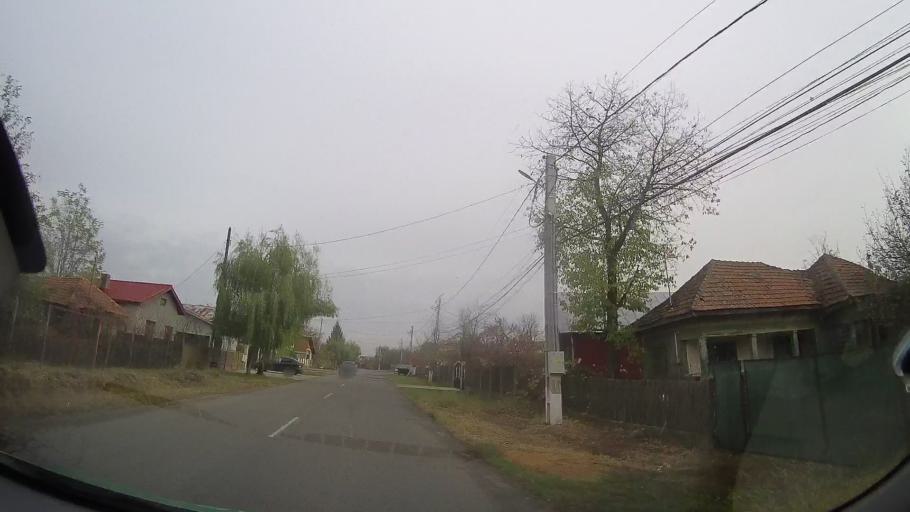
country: RO
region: Prahova
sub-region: Comuna Balta Doamnei
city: Balta Doamnei
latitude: 44.7597
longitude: 26.1623
